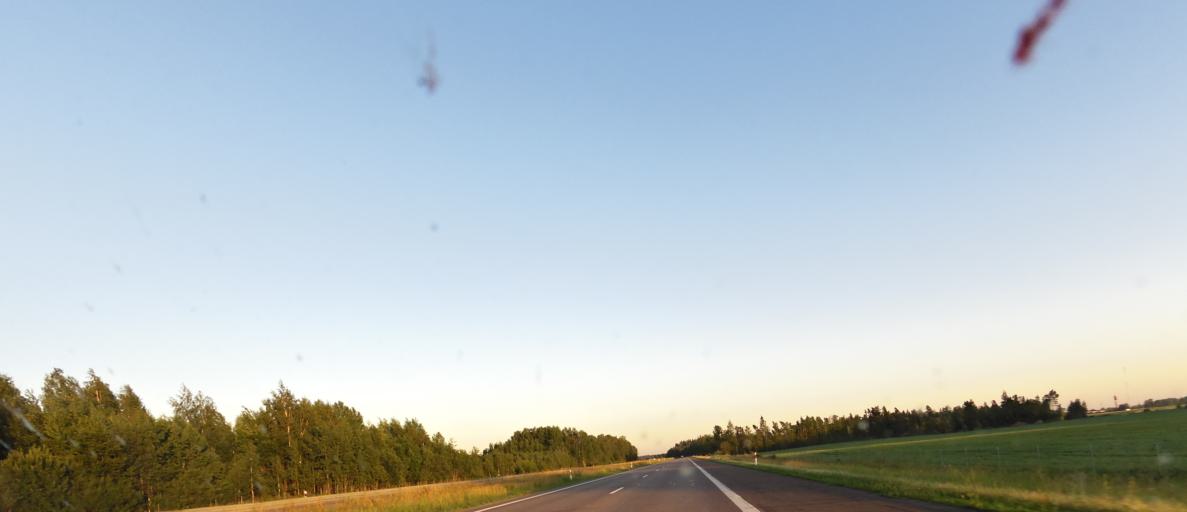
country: LT
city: Sirvintos
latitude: 55.0404
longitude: 24.8967
